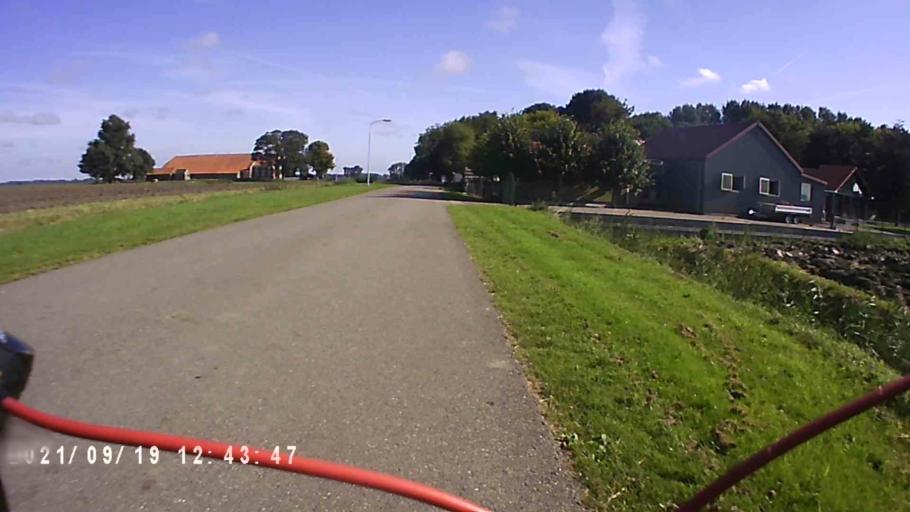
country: NL
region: Groningen
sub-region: Gemeente Delfzijl
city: Delfzijl
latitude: 53.2188
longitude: 6.9361
